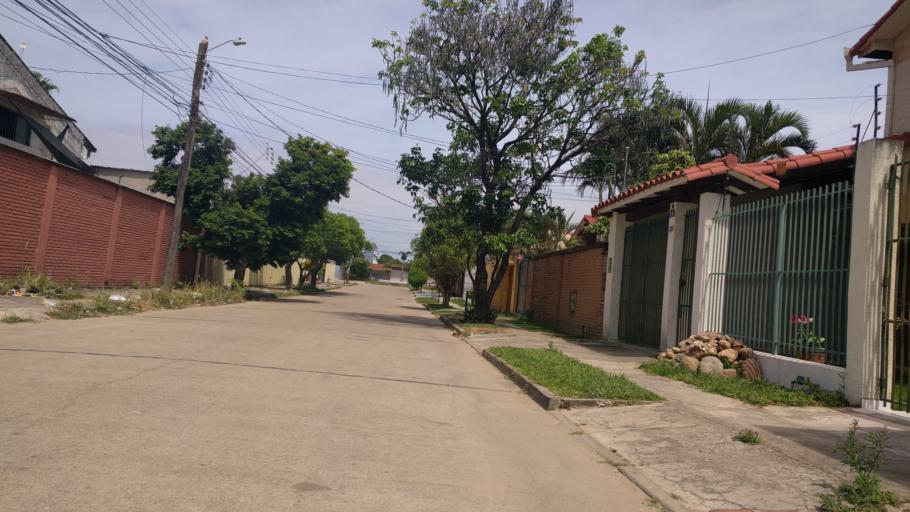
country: BO
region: Santa Cruz
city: Santa Cruz de la Sierra
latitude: -17.8191
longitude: -63.2221
